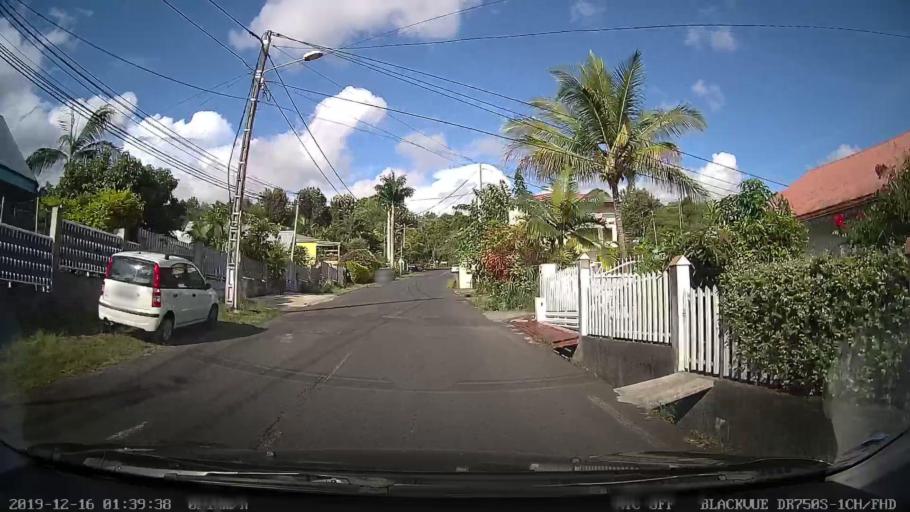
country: RE
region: Reunion
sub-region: Reunion
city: Le Tampon
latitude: -21.2617
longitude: 55.5081
